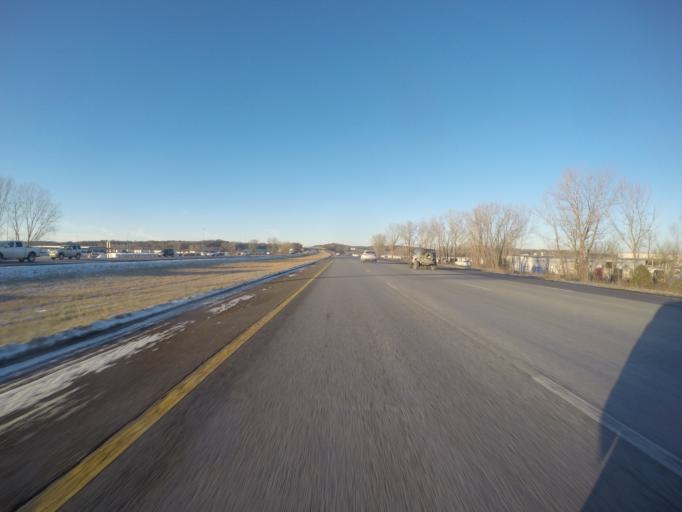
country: US
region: Kansas
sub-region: Wyandotte County
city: Edwardsville
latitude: 39.0546
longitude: -94.7903
